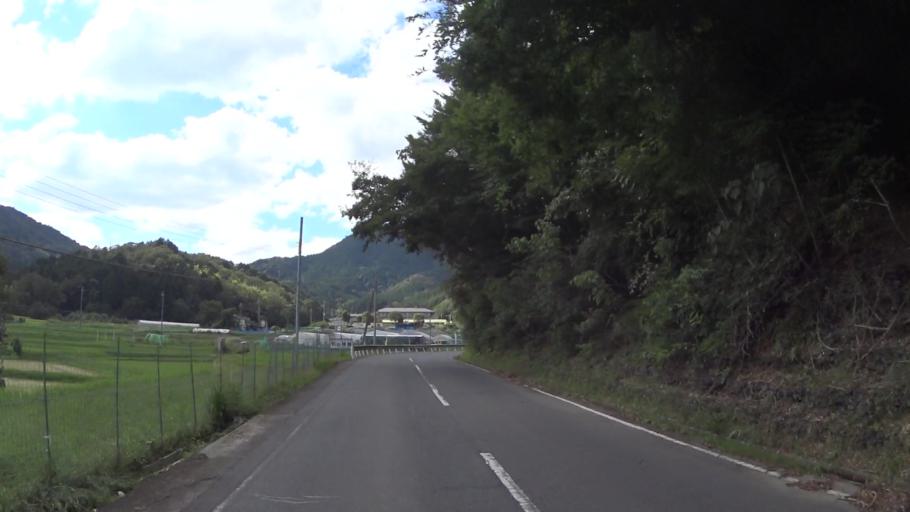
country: JP
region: Shiga Prefecture
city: Otsu-shi
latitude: 34.9475
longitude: 135.8902
